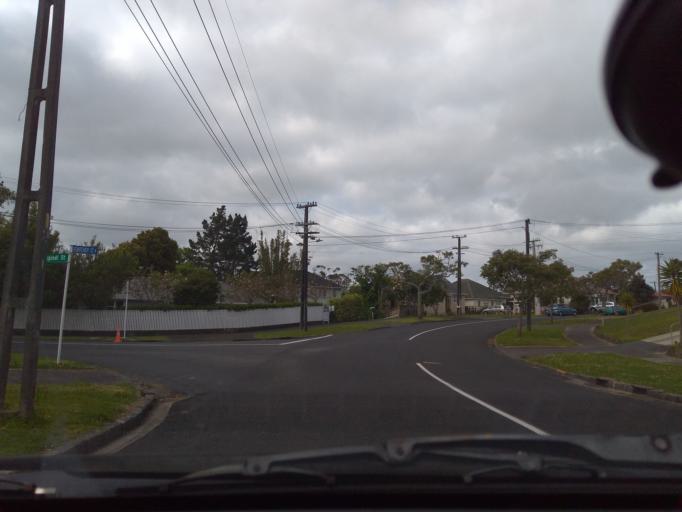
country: NZ
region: Auckland
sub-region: Auckland
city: Rosebank
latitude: -36.8760
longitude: 174.7146
